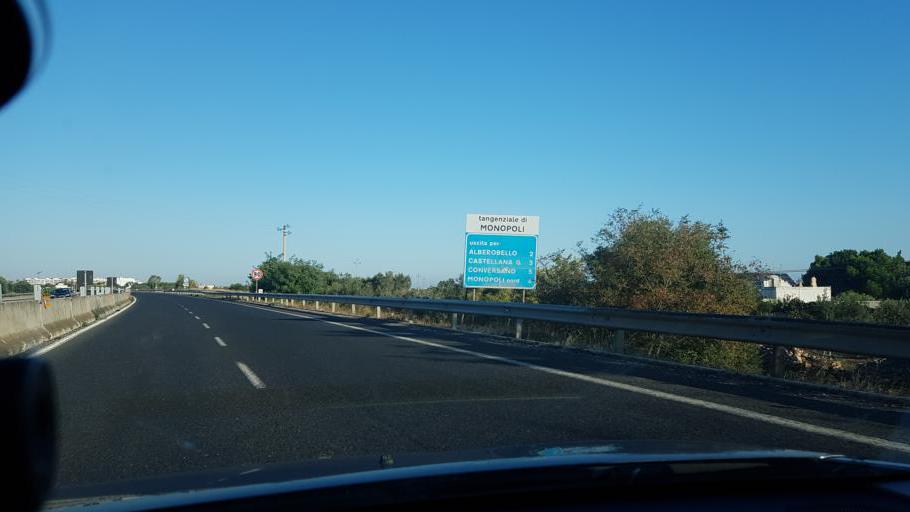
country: IT
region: Apulia
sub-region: Provincia di Bari
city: Monopoli
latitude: 40.9238
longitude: 17.3140
